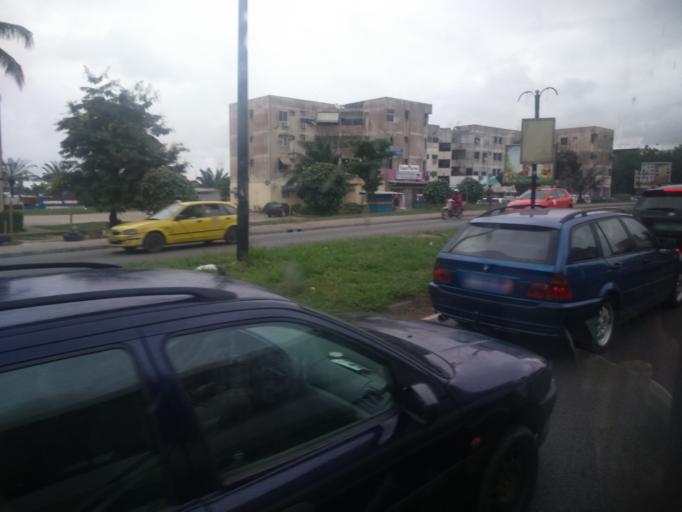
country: CI
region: Lagunes
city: Abobo
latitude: 5.3710
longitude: -3.9983
